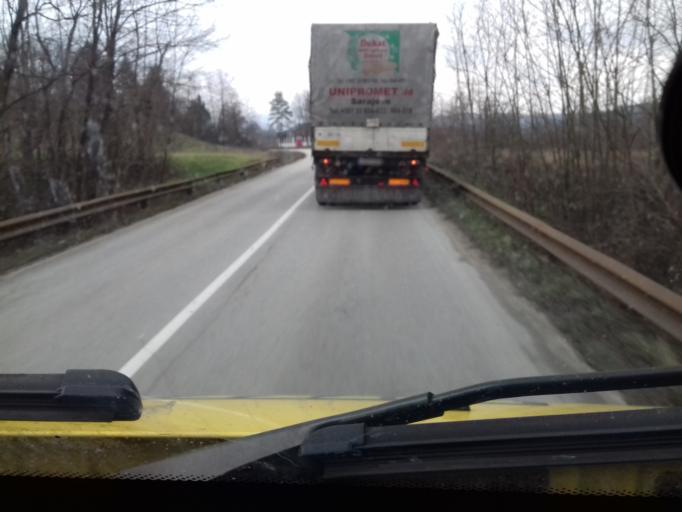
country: BA
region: Federation of Bosnia and Herzegovina
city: Dubravica
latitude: 44.4192
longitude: 18.0972
